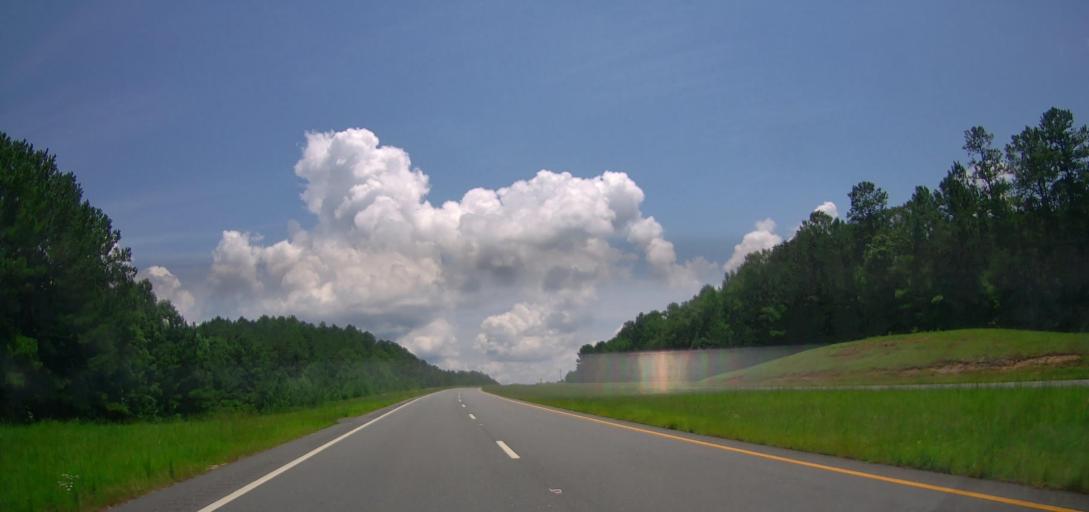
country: US
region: Georgia
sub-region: Upson County
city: Thomaston
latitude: 32.7929
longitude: -84.2584
